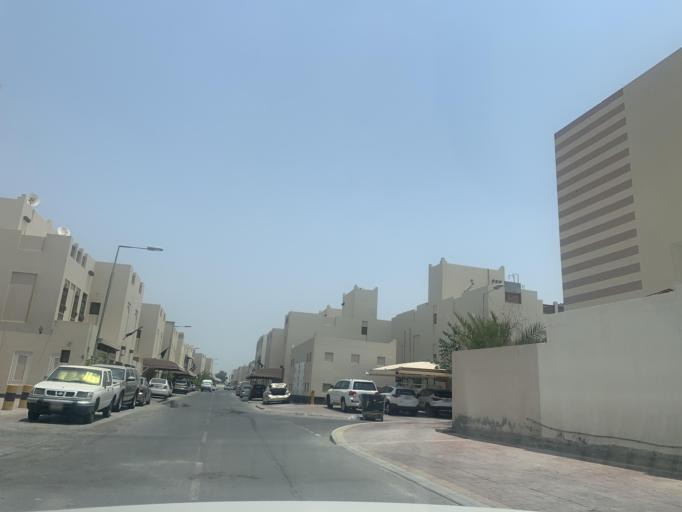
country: BH
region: Central Governorate
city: Madinat Hamad
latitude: 26.1462
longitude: 50.4608
